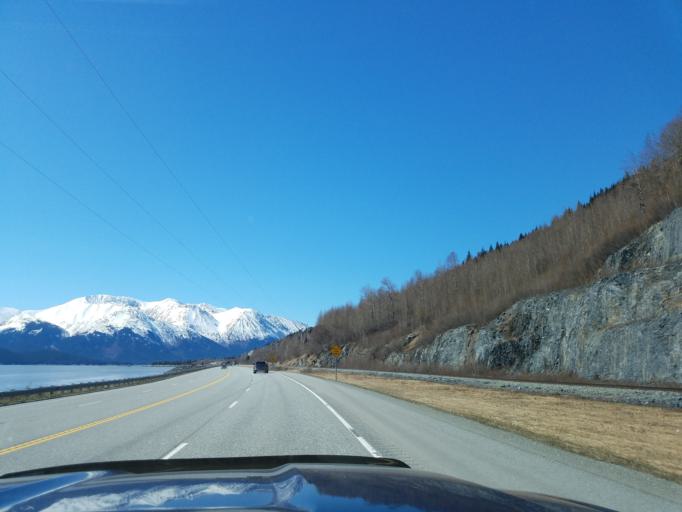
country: US
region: Alaska
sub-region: Anchorage Municipality
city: Girdwood
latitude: 60.9346
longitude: -149.3119
